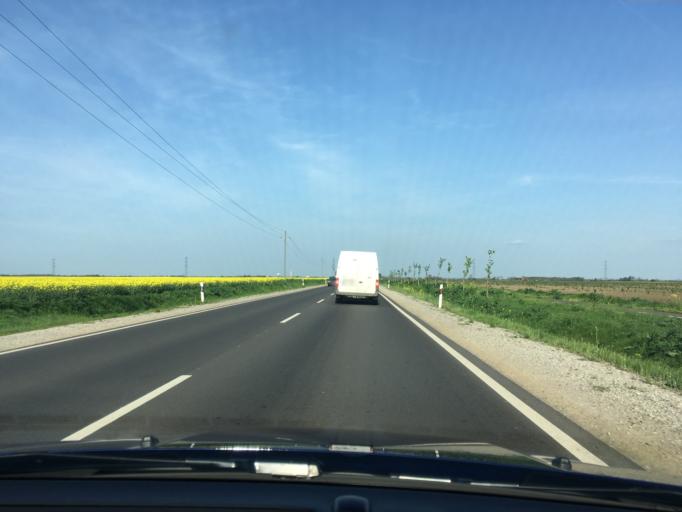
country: HU
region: Bekes
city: Ujkigyos
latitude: 46.6657
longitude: 20.9678
